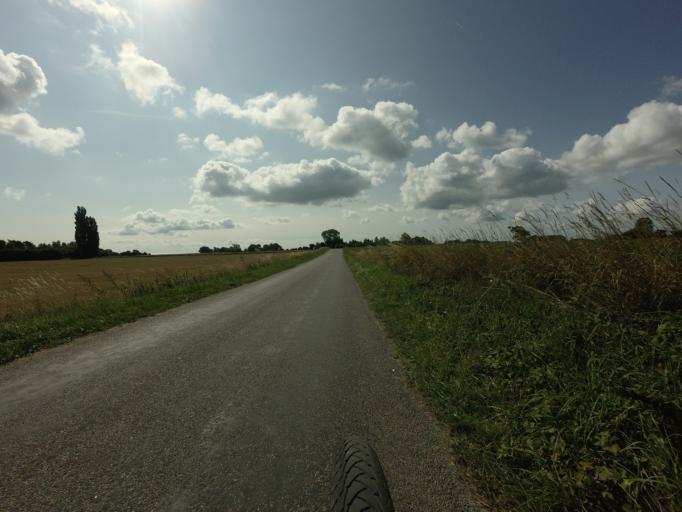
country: DK
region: Zealand
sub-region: Vordingborg Kommune
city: Stege
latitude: 54.9698
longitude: 12.3392
